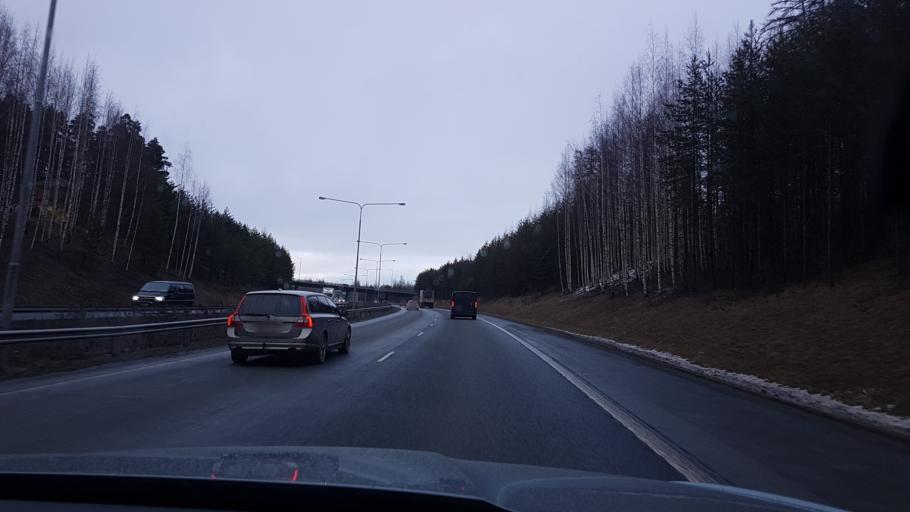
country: FI
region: Pirkanmaa
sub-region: Tampere
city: Tampere
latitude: 61.4715
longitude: 23.8635
